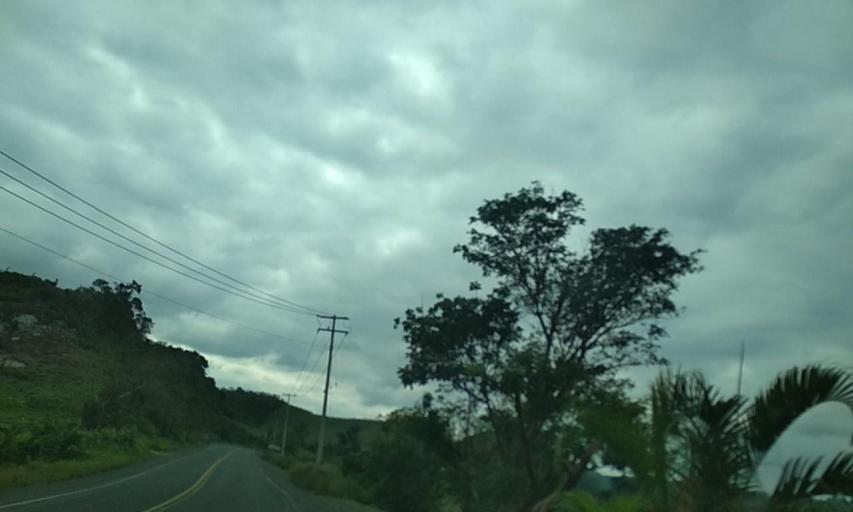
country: MX
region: Veracruz
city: Papantla de Olarte
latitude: 20.4691
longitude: -97.3183
